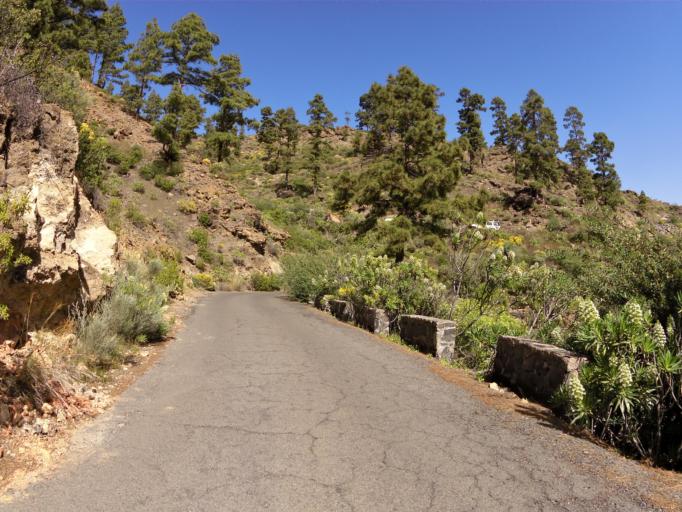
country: ES
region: Canary Islands
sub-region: Provincia de Las Palmas
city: Mogan
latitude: 27.8991
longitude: -15.6867
